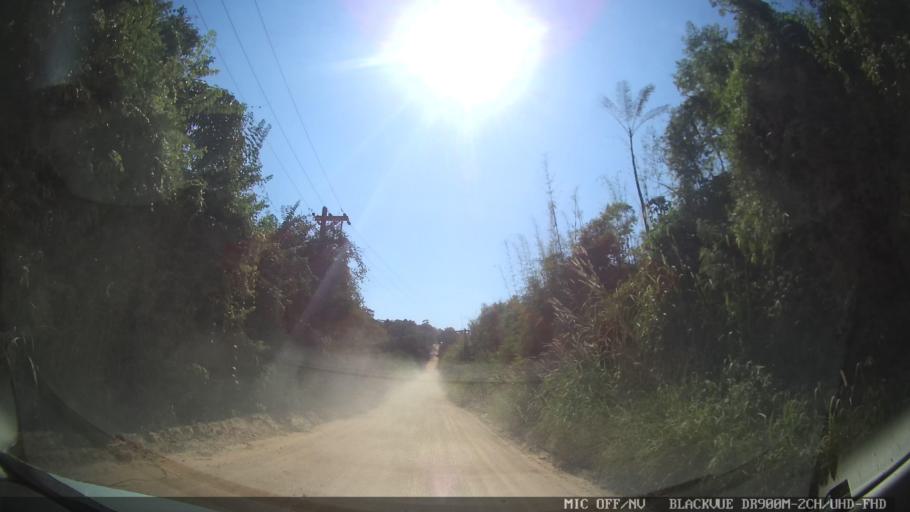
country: BR
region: Sao Paulo
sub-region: Itupeva
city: Itupeva
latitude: -23.1043
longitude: -47.0855
